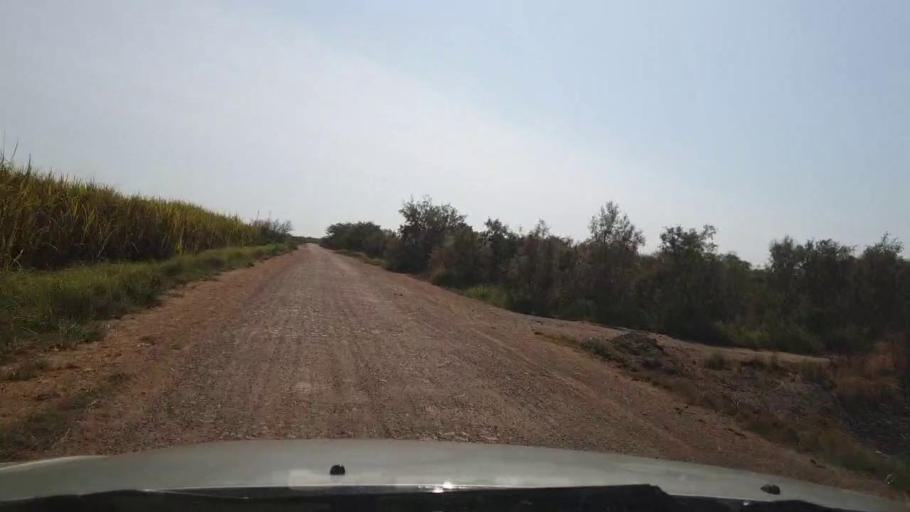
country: PK
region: Sindh
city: Bulri
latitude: 24.9992
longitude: 68.3188
